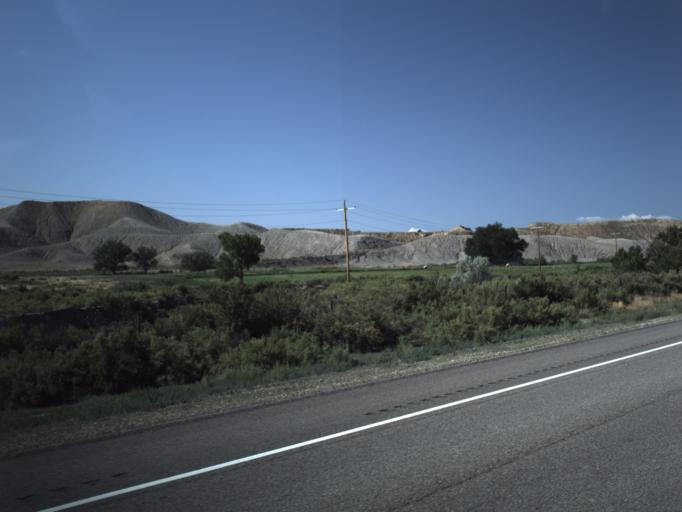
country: US
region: Utah
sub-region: Emery County
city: Orangeville
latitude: 39.1592
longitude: -111.0741
